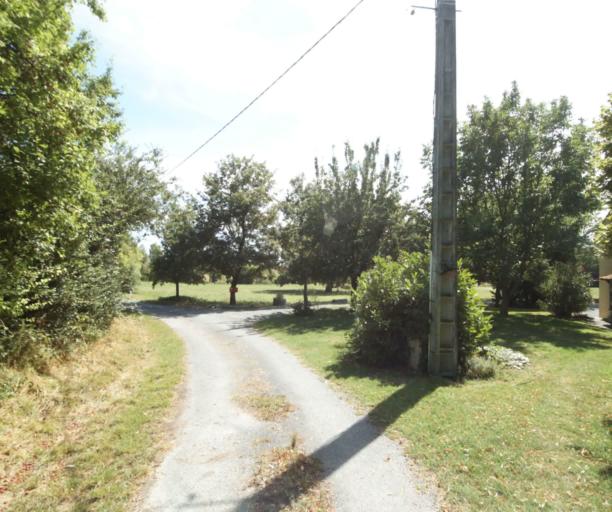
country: FR
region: Midi-Pyrenees
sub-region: Departement du Tarn
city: Puylaurens
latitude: 43.5346
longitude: 2.0210
